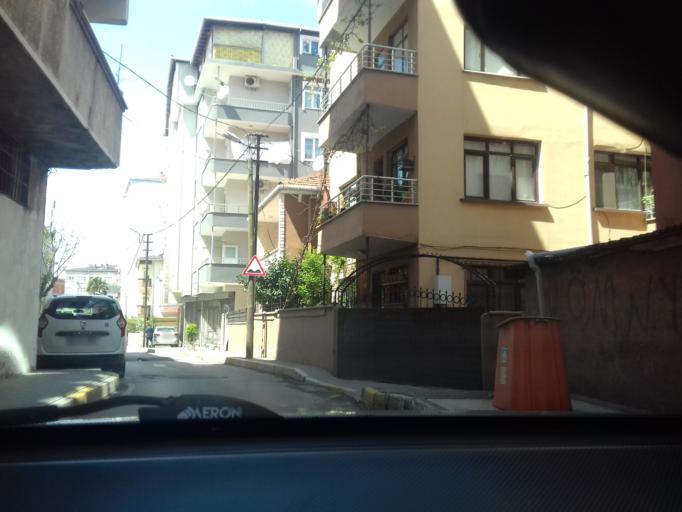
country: TR
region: Istanbul
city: Pendik
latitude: 40.8726
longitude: 29.2697
